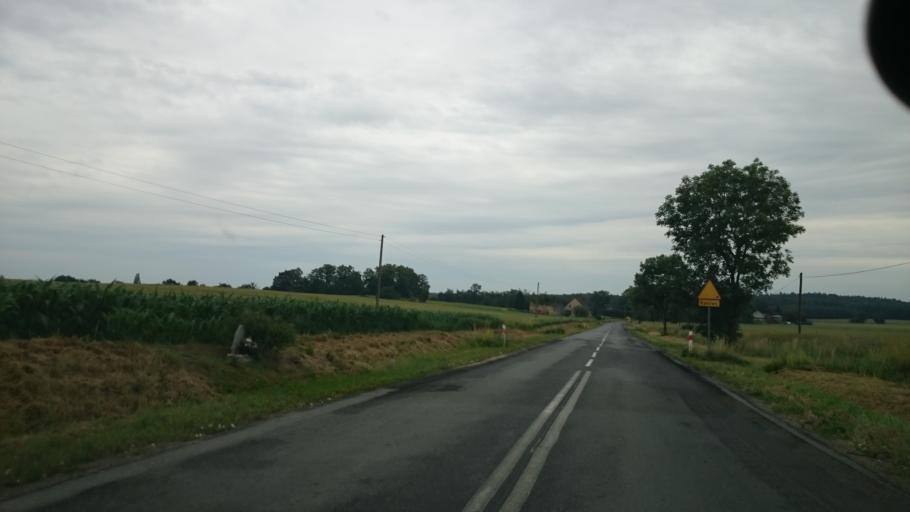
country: PL
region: Lower Silesian Voivodeship
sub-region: Powiat strzelinski
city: Przeworno
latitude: 50.6436
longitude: 17.2190
